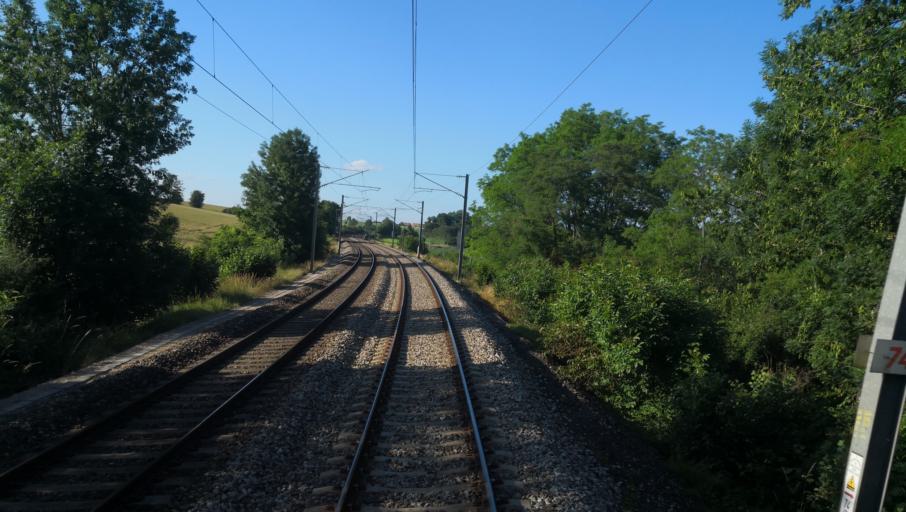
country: FR
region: Ile-de-France
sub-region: Departement des Yvelines
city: Breval
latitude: 48.9204
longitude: 1.5183
